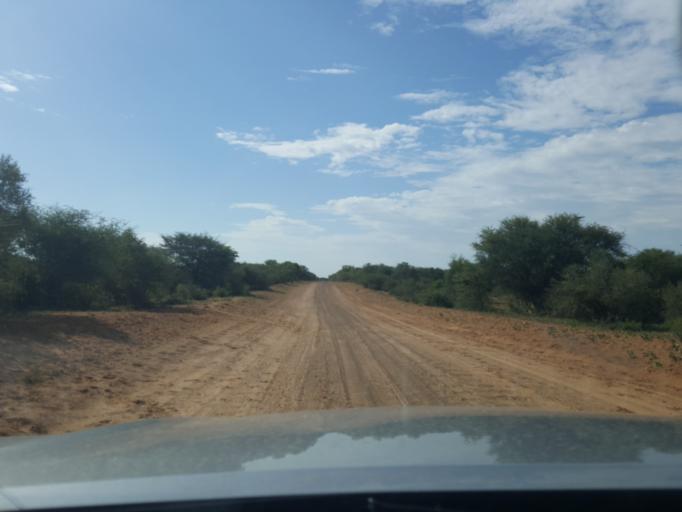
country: BW
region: Kweneng
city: Khudumelapye
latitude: -23.5372
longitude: 24.7276
